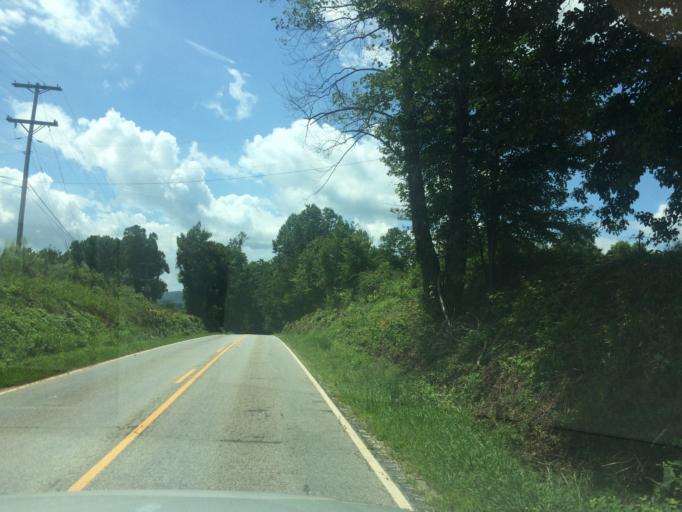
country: US
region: North Carolina
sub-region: Rutherford County
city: Lake Lure
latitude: 35.3534
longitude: -82.1806
